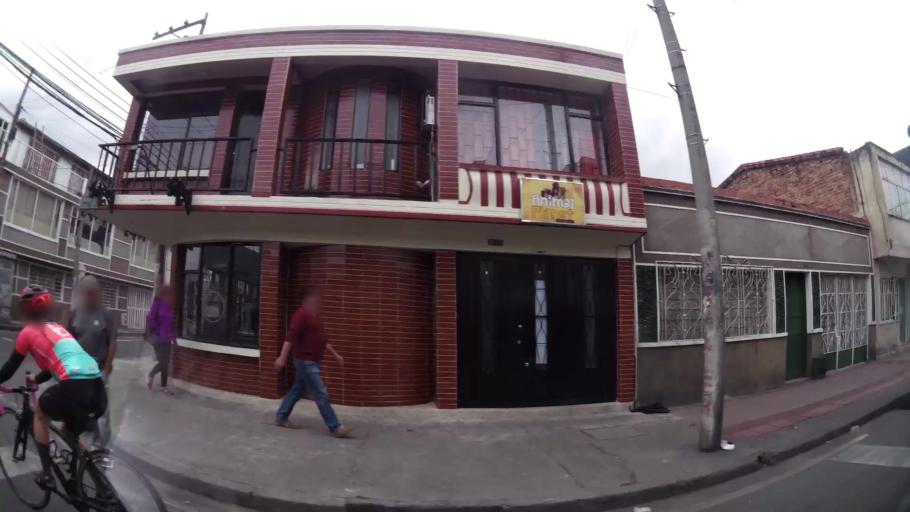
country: CO
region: Bogota D.C.
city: Bogota
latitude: 4.6716
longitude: -74.0983
